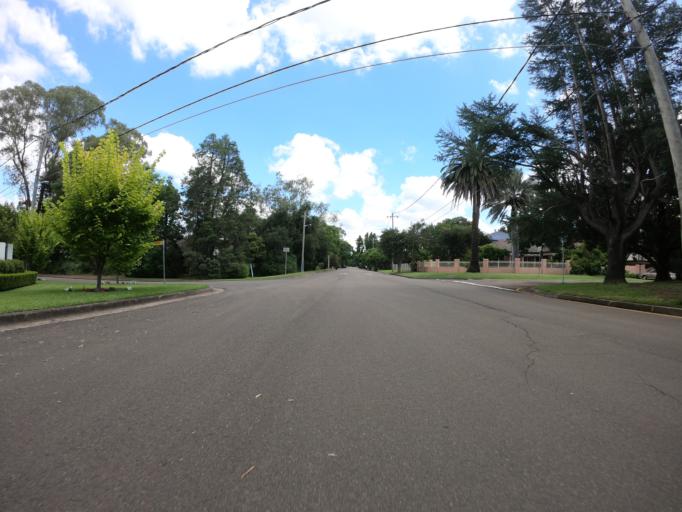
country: AU
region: New South Wales
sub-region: Penrith Municipality
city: Penrith
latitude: -33.7521
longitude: 150.6780
